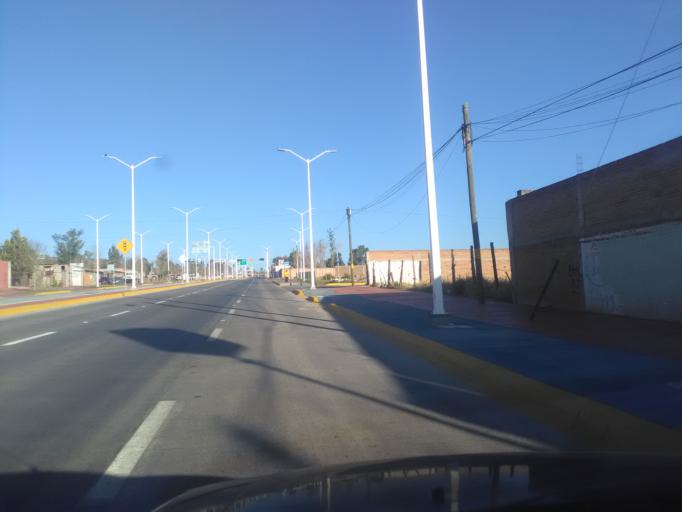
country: MX
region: Durango
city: Victoria de Durango
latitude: 23.9931
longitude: -104.7129
